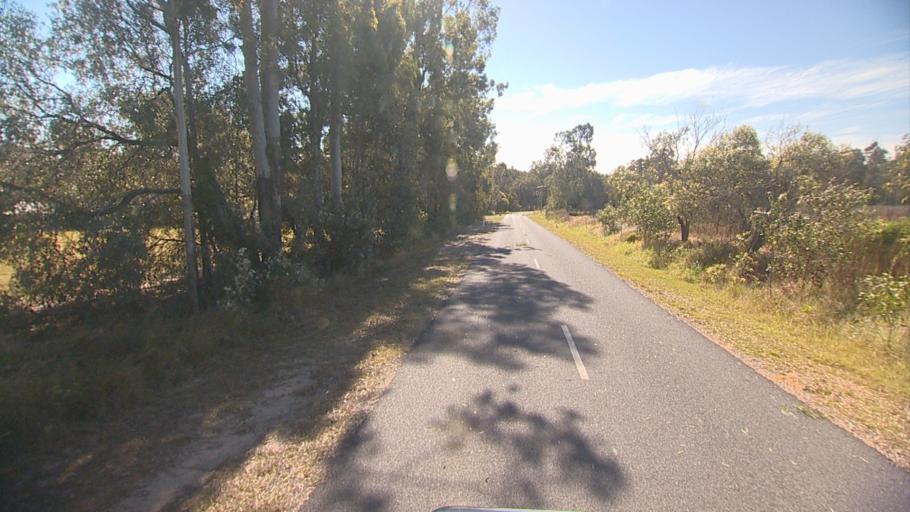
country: AU
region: Queensland
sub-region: Ipswich
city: Springfield Lakes
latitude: -27.7199
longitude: 152.9371
